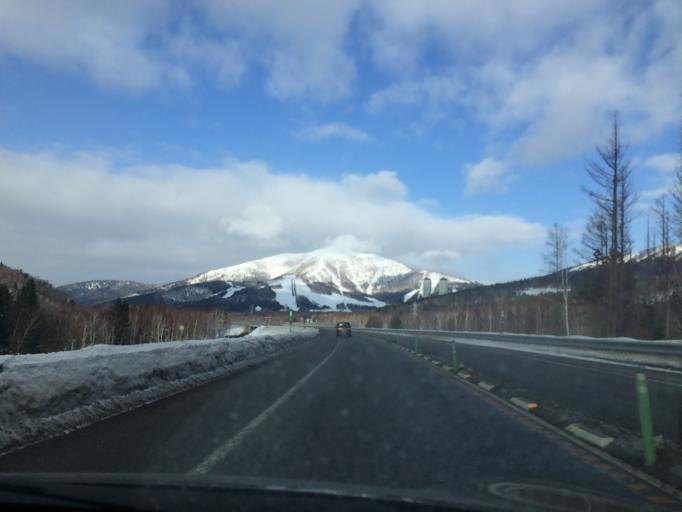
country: JP
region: Hokkaido
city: Shimo-furano
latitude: 43.0508
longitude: 142.6482
